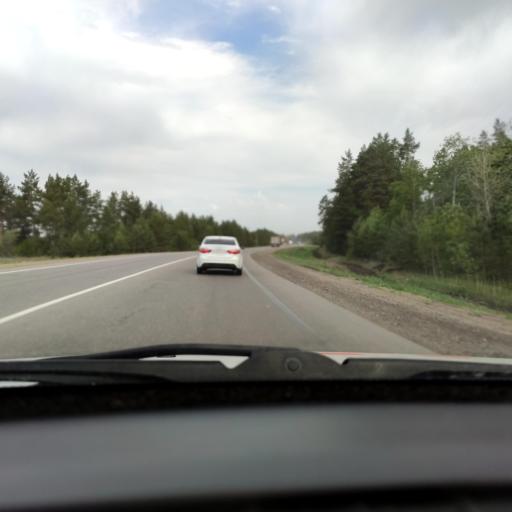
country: RU
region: Samara
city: Mirnyy
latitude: 53.5303
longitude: 50.3056
